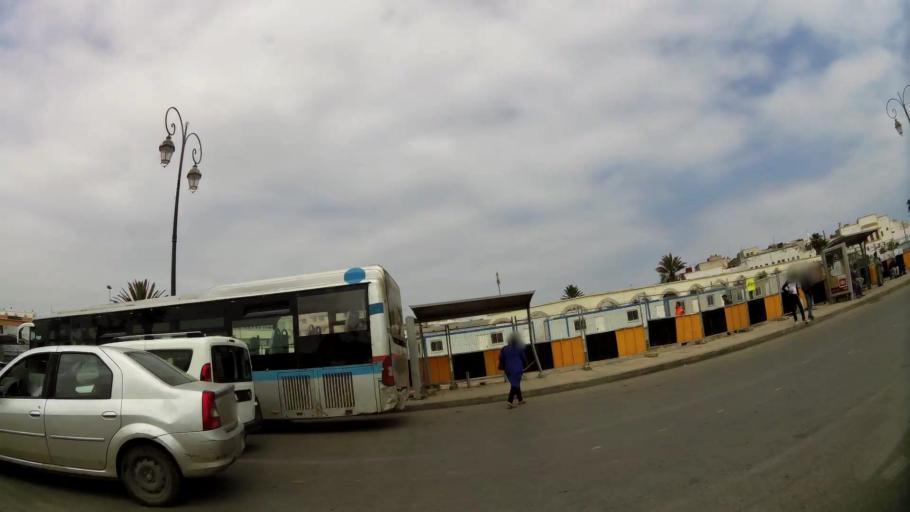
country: MA
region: Rabat-Sale-Zemmour-Zaer
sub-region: Rabat
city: Rabat
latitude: 34.0223
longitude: -6.8413
